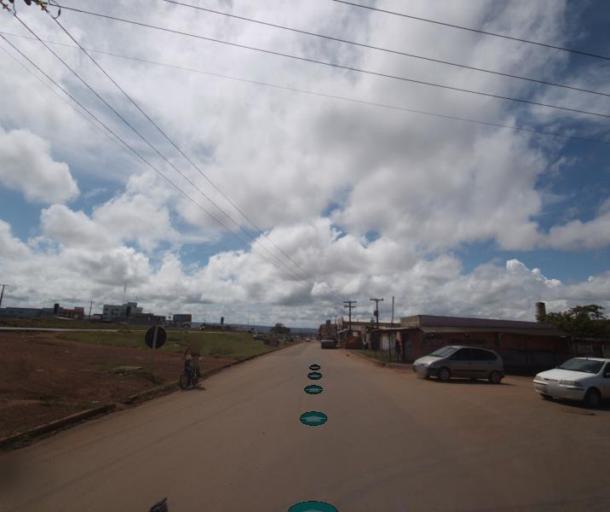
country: BR
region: Federal District
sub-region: Brasilia
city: Brasilia
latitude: -15.7366
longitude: -48.2856
